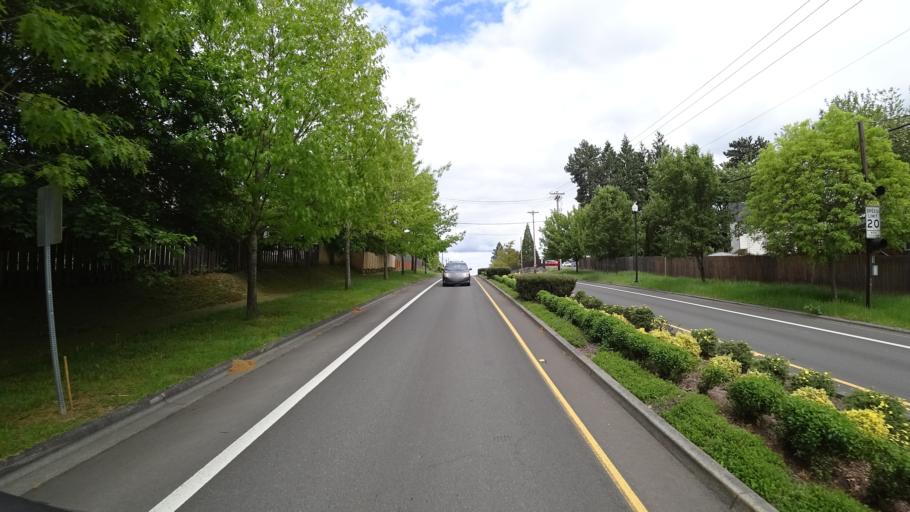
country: US
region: Oregon
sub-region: Washington County
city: Aloha
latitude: 45.4634
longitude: -122.8518
